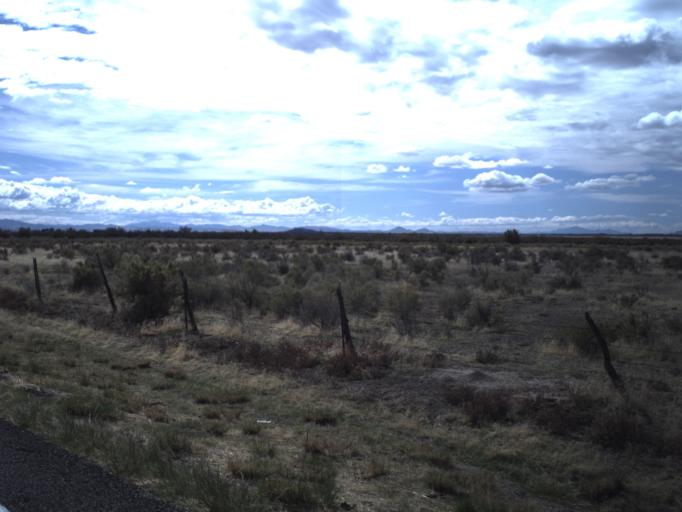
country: US
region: Utah
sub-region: Millard County
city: Fillmore
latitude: 39.0717
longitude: -112.4098
